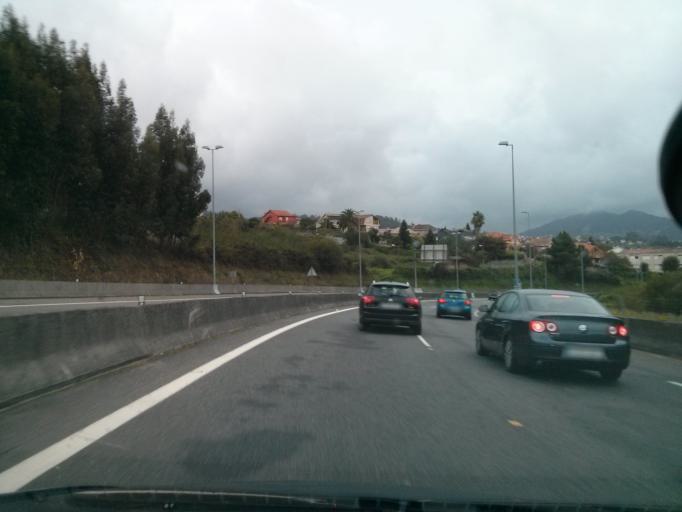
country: ES
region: Galicia
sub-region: Provincia de Pontevedra
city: Vigo
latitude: 42.2080
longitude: -8.6884
